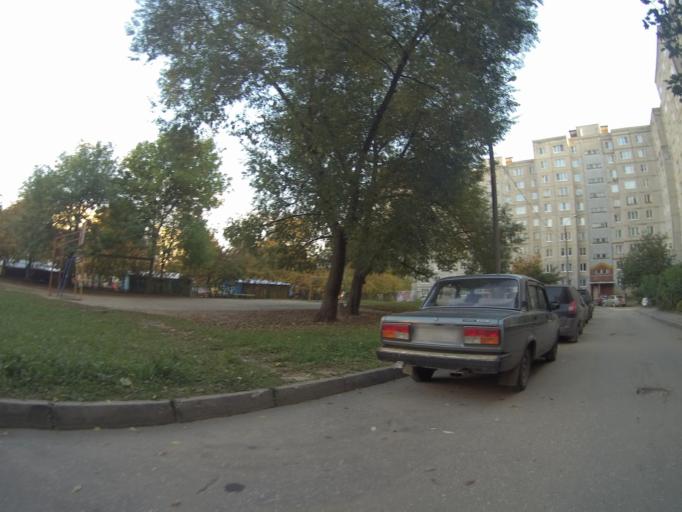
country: RU
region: Vladimir
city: Vladimir
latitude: 56.1036
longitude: 40.3478
